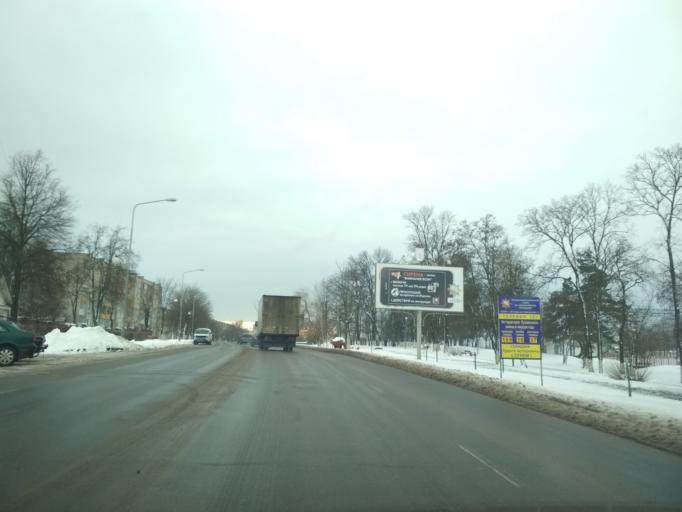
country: BY
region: Minsk
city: Mar''ina Horka
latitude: 53.5167
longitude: 28.1401
